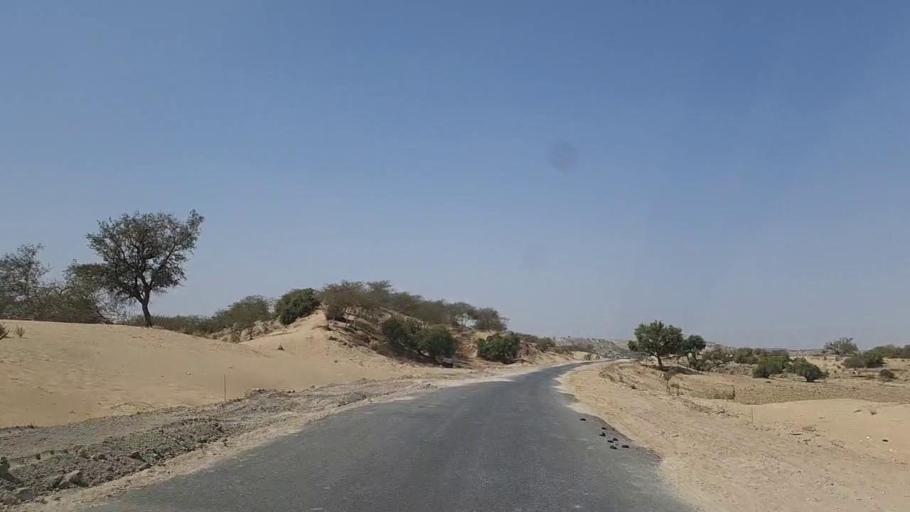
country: PK
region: Sindh
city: Diplo
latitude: 24.5869
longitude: 69.5366
